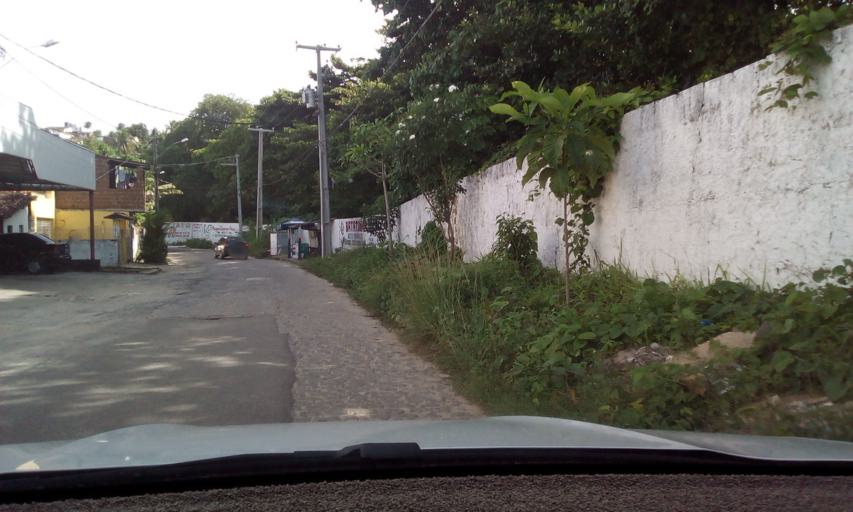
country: BR
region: Paraiba
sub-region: Joao Pessoa
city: Joao Pessoa
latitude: -7.1333
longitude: -34.8879
